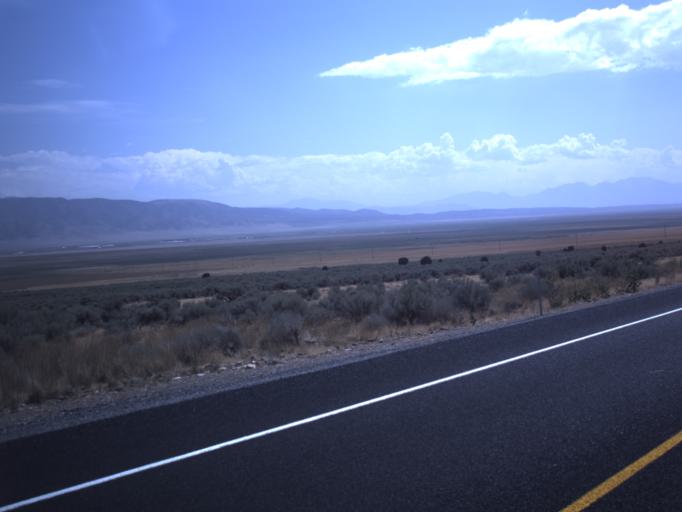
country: US
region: Utah
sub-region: Utah County
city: Eagle Mountain
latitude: 40.3117
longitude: -112.1021
